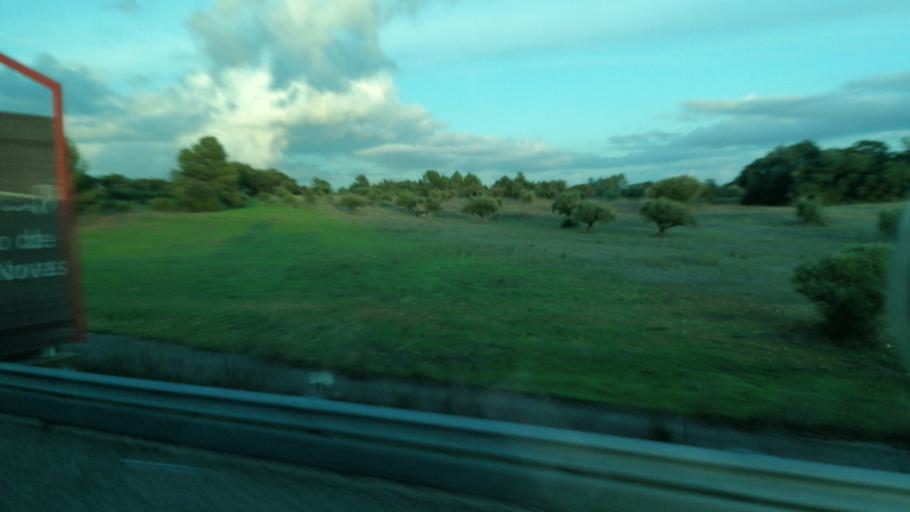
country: PT
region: Santarem
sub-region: Alcanena
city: Alcanena
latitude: 39.4317
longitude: -8.6278
